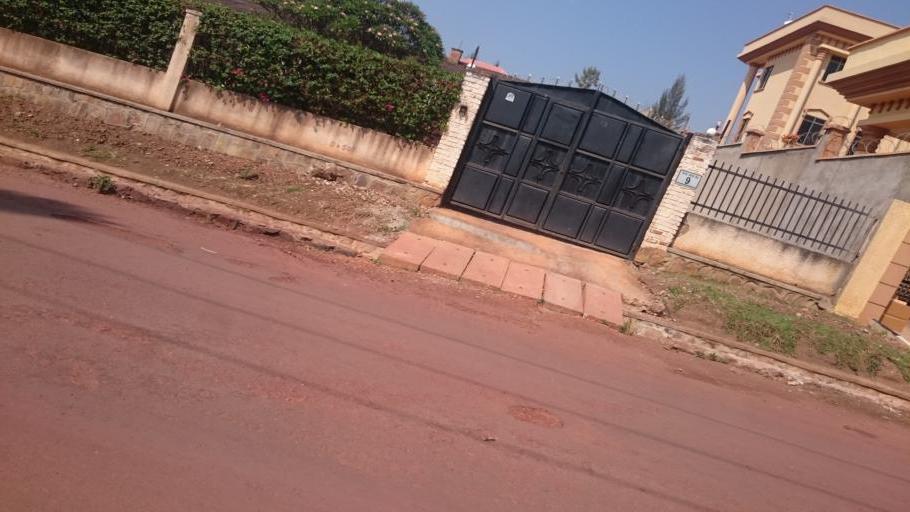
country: RW
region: Kigali
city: Kigali
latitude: -1.9394
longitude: 30.0876
